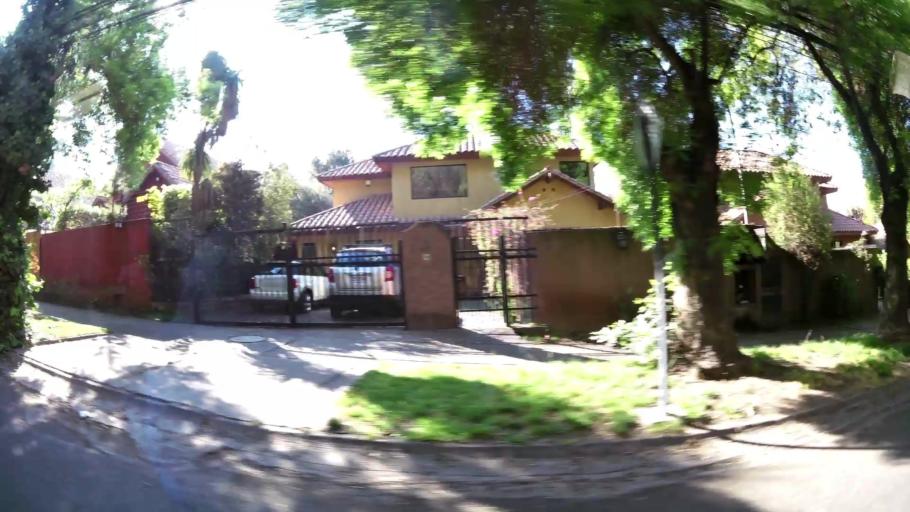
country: CL
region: Santiago Metropolitan
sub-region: Provincia de Chacabuco
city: Chicureo Abajo
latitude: -33.3405
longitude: -70.6682
